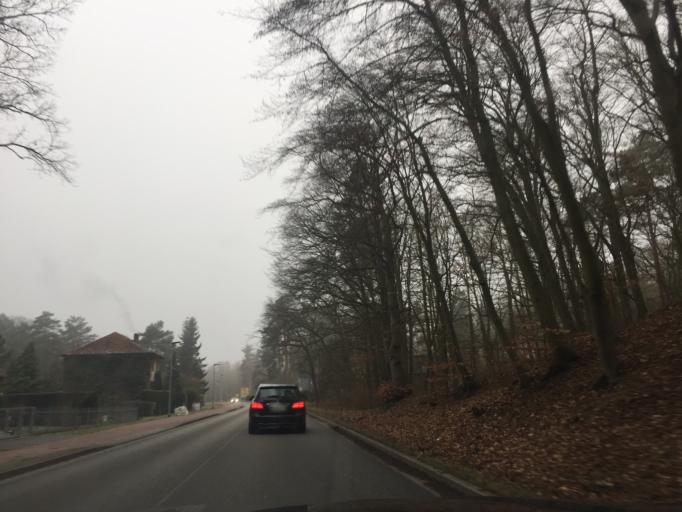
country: DE
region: Brandenburg
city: Falkensee
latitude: 52.6006
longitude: 13.1043
